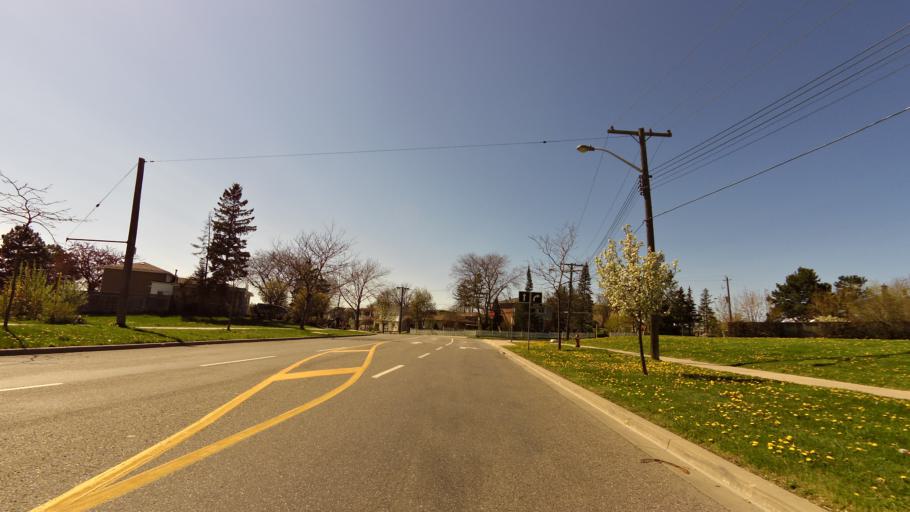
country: CA
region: Ontario
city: Concord
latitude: 43.7616
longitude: -79.5209
